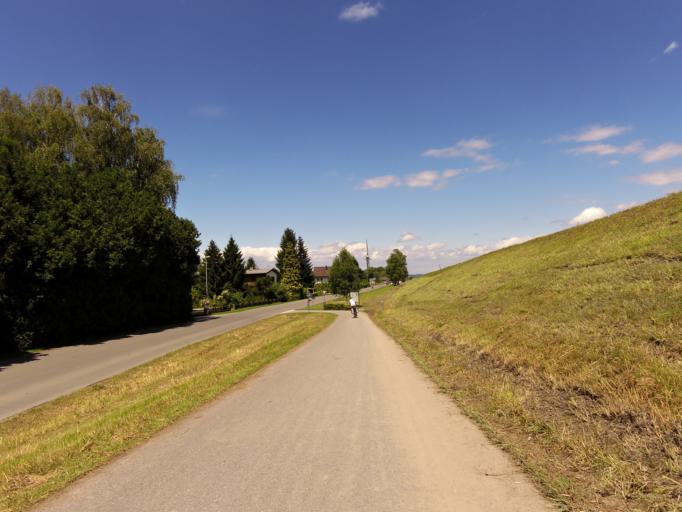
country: AT
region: Vorarlberg
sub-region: Politischer Bezirk Bregenz
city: Fussach
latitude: 47.4824
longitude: 9.6678
